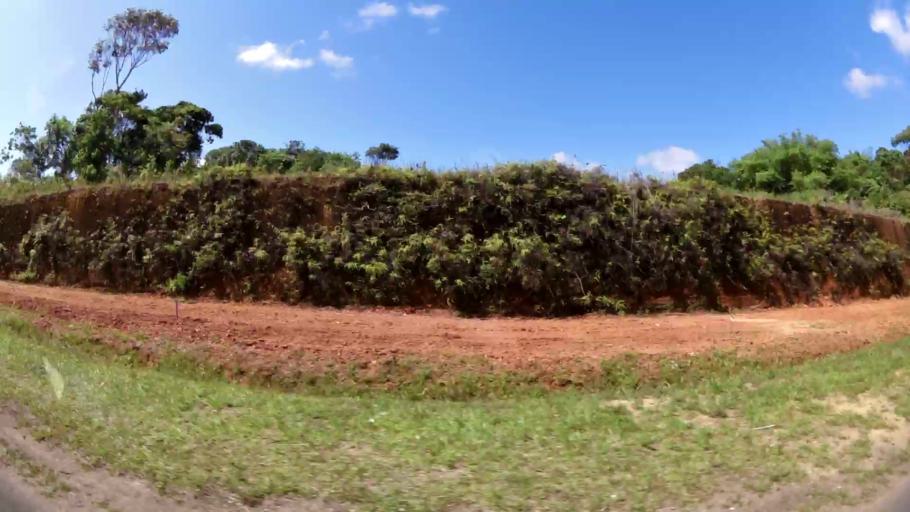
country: GF
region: Guyane
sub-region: Guyane
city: Matoury
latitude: 4.8341
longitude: -52.3269
